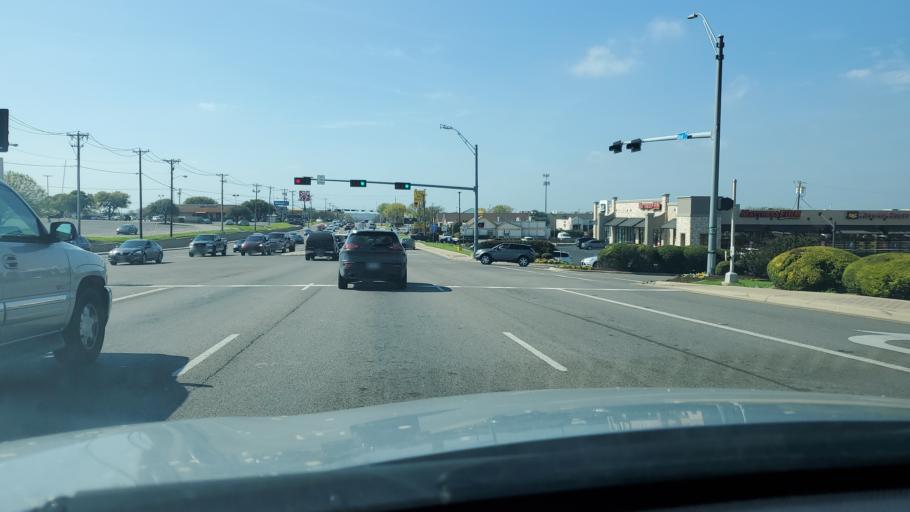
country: US
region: Texas
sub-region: Bell County
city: Temple
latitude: 31.0712
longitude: -97.3689
